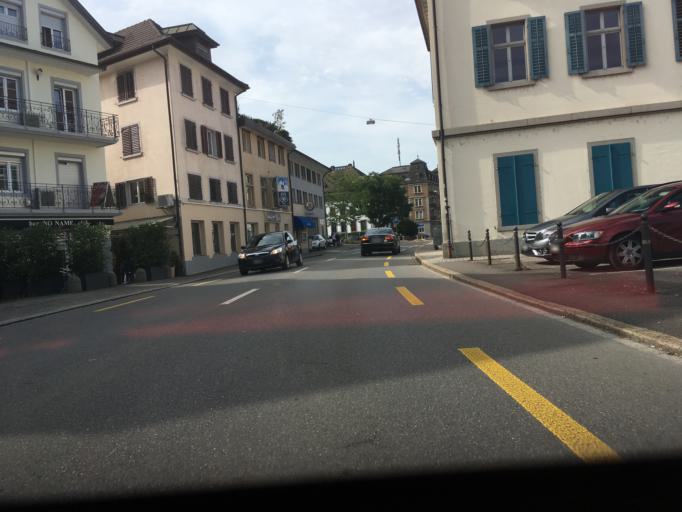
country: CH
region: Zurich
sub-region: Bezirk Horgen
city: Waedenswil / Dorf (Waedenswil)
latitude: 47.2275
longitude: 8.6759
